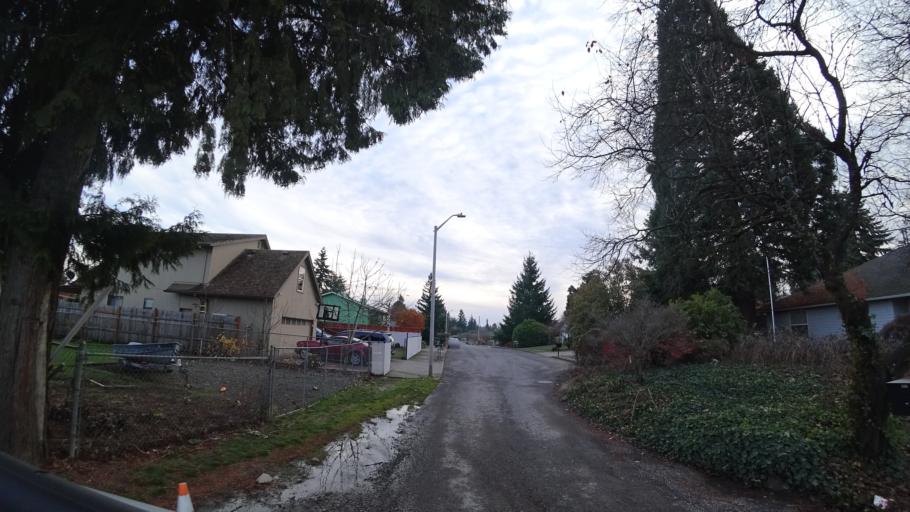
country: US
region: Oregon
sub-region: Multnomah County
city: Lents
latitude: 45.5179
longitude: -122.5172
